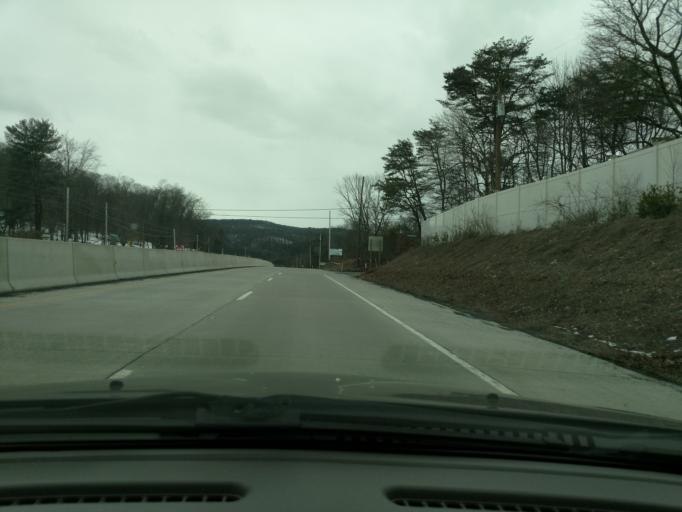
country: US
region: Pennsylvania
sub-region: Schuylkill County
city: Orwigsburg
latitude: 40.6163
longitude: -76.0450
